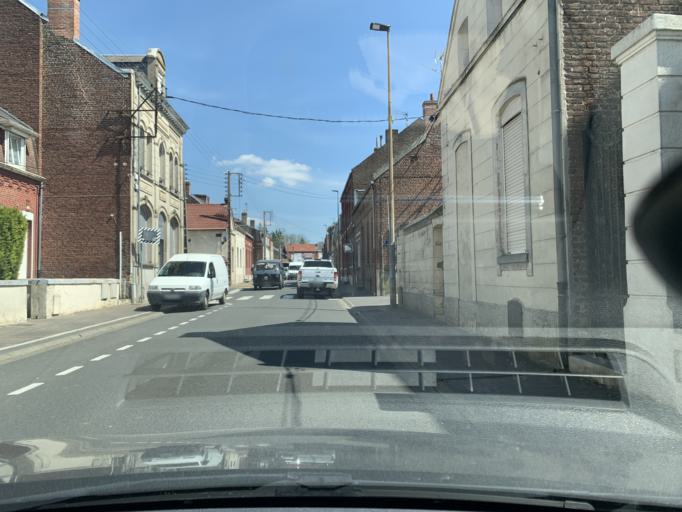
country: FR
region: Nord-Pas-de-Calais
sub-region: Departement du Nord
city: Caudry
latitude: 50.1173
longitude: 3.4083
